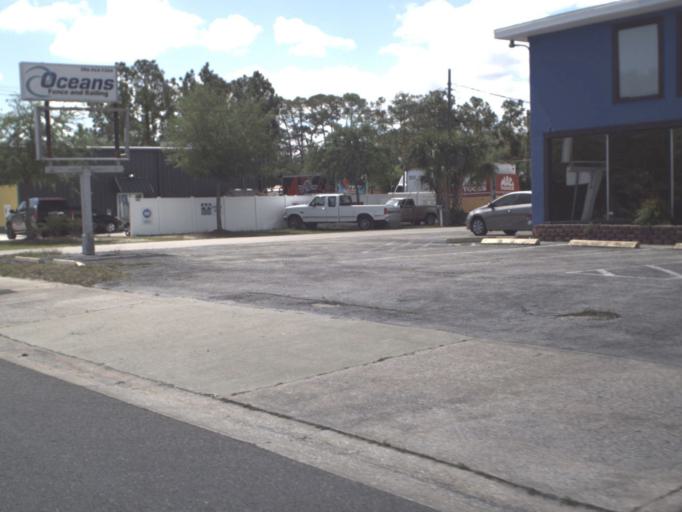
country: US
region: Florida
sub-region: Flagler County
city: Bunnell
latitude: 29.4700
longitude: -81.2641
